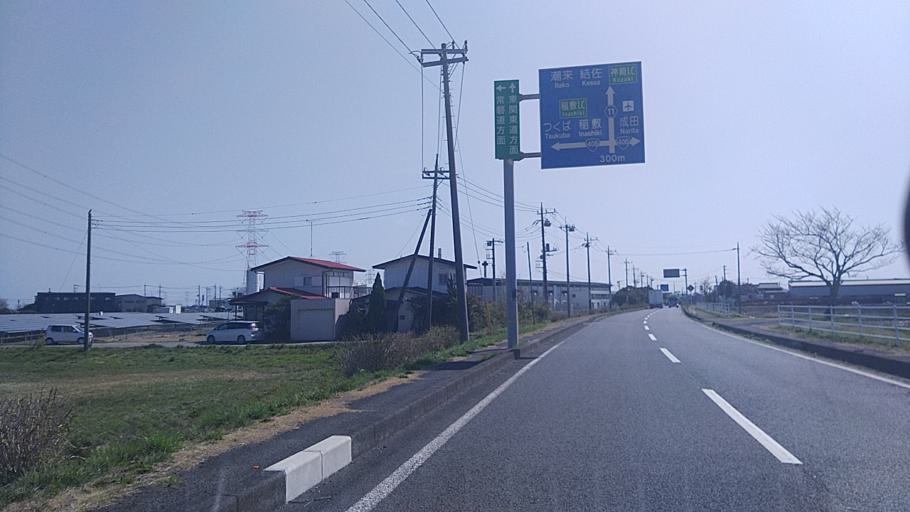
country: JP
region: Ibaraki
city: Edosaki
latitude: 35.8795
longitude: 140.2916
